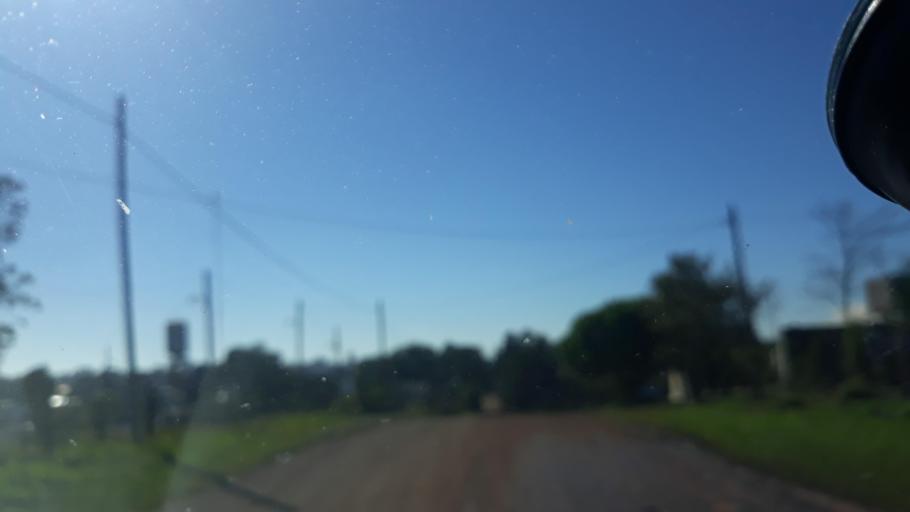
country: AR
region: Misiones
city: Bernardo de Irigoyen
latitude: -26.2630
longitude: -53.6495
